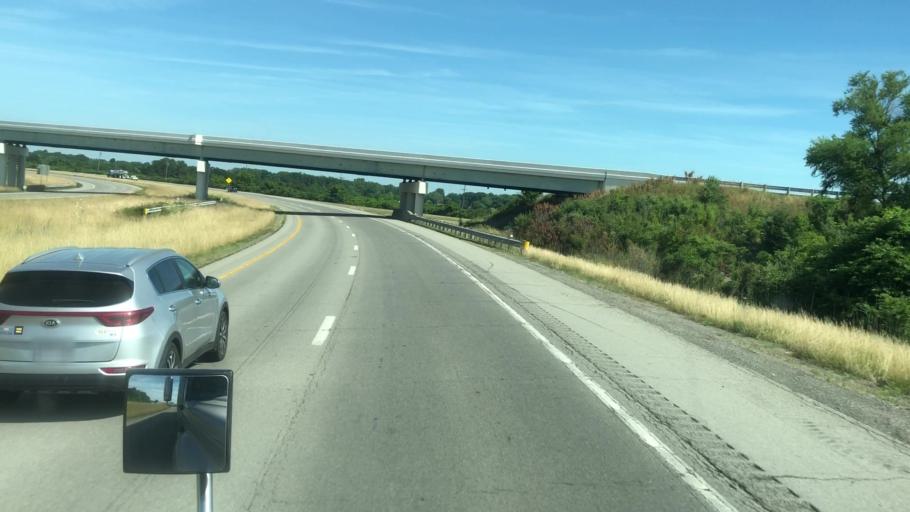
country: US
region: Ohio
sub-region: Erie County
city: Huron
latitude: 41.3970
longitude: -82.5744
